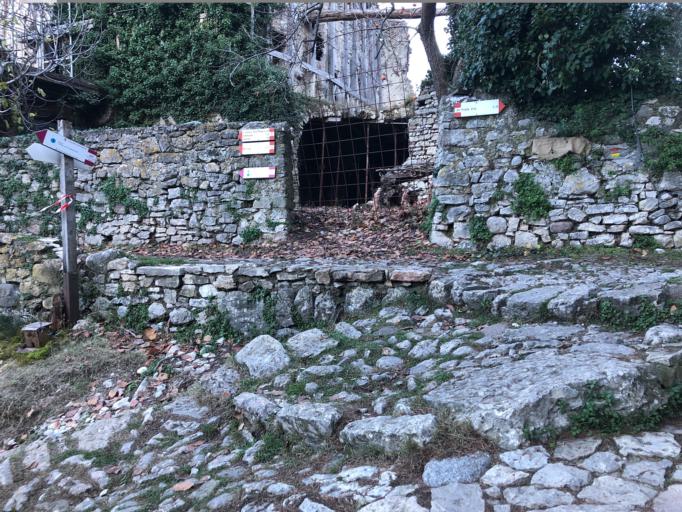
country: IT
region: Veneto
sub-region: Provincia di Verona
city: Magugnano
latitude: 45.6966
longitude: 10.7641
